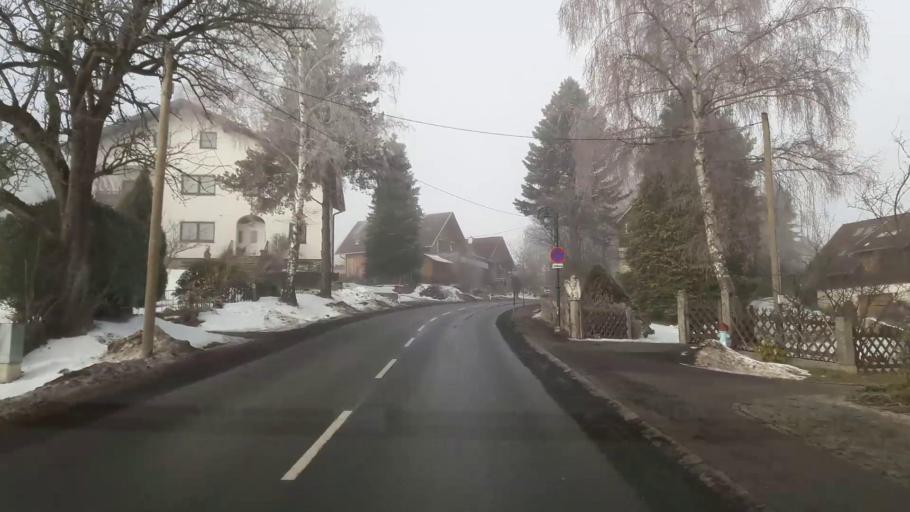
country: AT
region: Lower Austria
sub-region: Politischer Bezirk Neunkirchen
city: Sankt Corona am Wechsel
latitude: 47.5773
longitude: 16.0236
